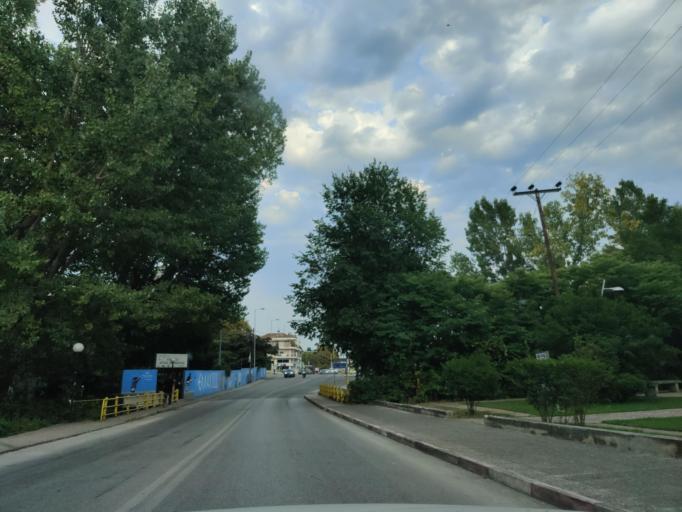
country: GR
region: East Macedonia and Thrace
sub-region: Nomos Dramas
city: Drama
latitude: 41.1487
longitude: 24.1402
